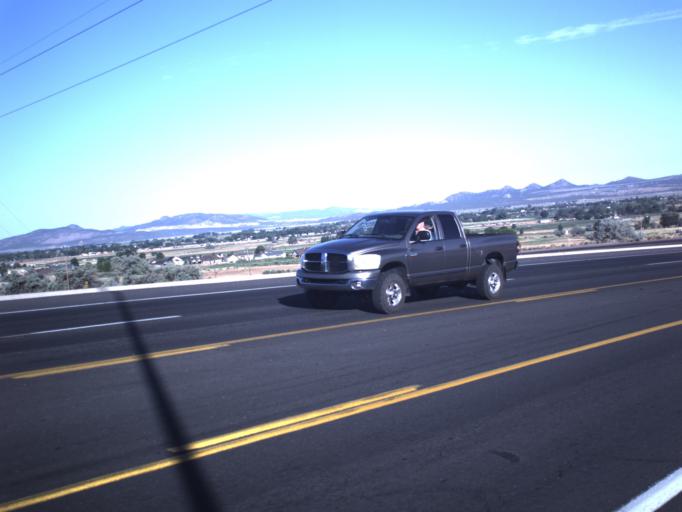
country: US
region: Utah
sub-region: Iron County
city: Cedar City
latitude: 37.7293
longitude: -113.0543
